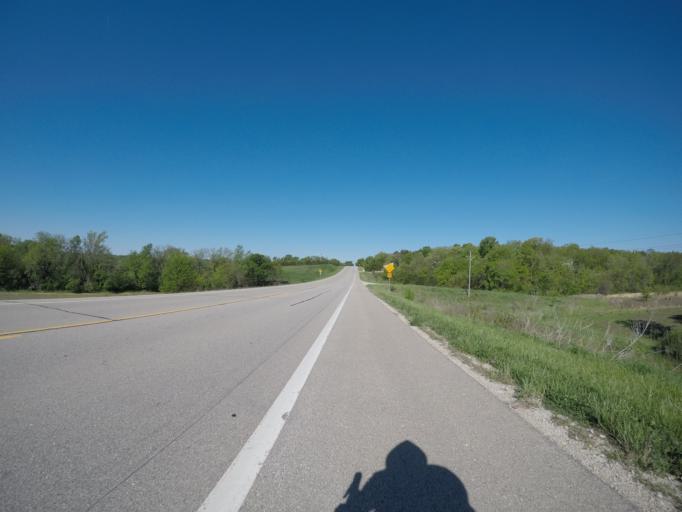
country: US
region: Kansas
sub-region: Douglas County
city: Lawrence
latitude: 38.9714
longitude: -95.4483
